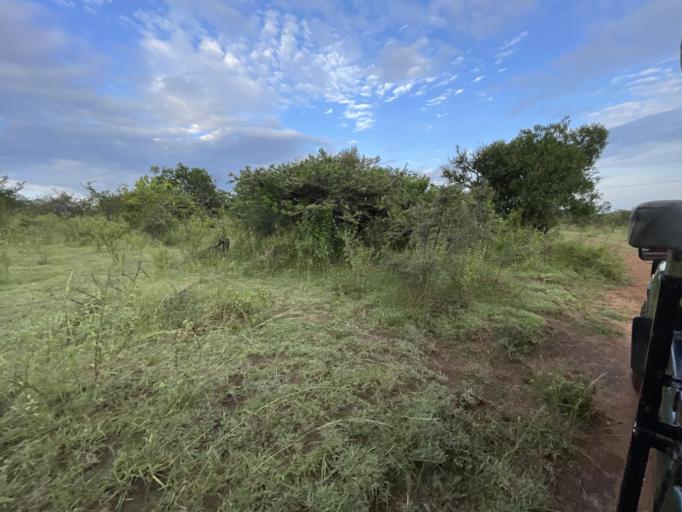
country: TZ
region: Mara
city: Mugumu
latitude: -1.7032
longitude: 35.3089
